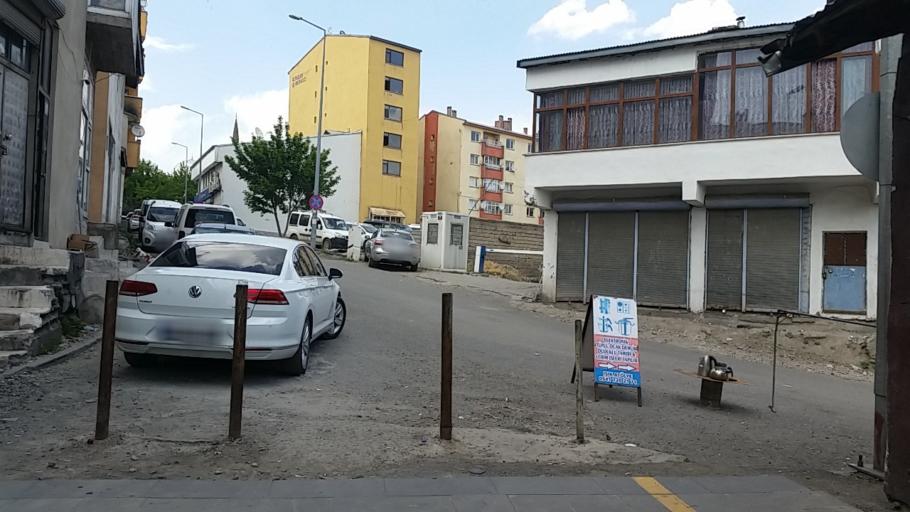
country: TR
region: Agri
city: Agri
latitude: 39.7182
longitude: 43.0517
